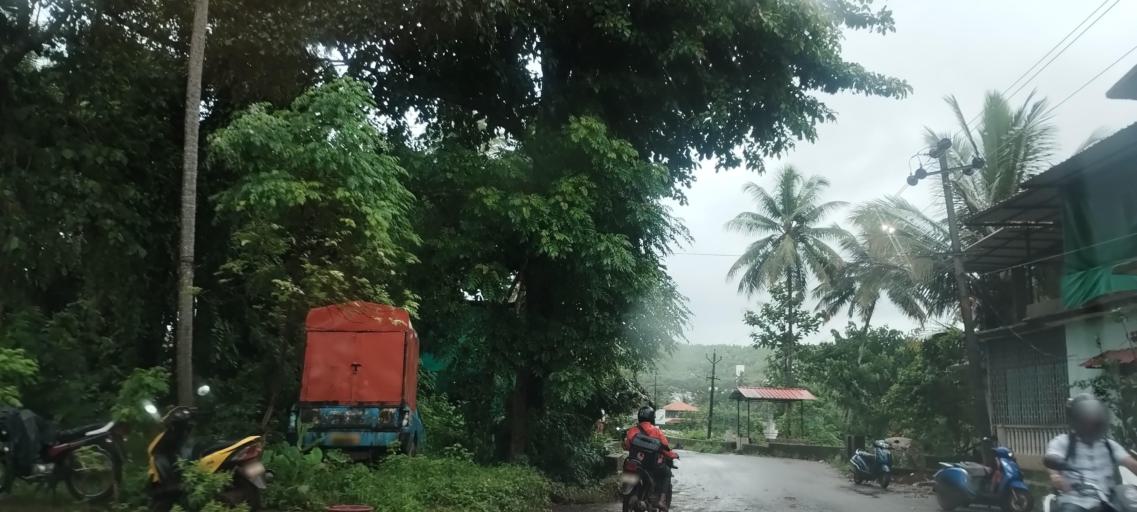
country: IN
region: Goa
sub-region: North Goa
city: Solim
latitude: 15.5949
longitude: 73.7723
